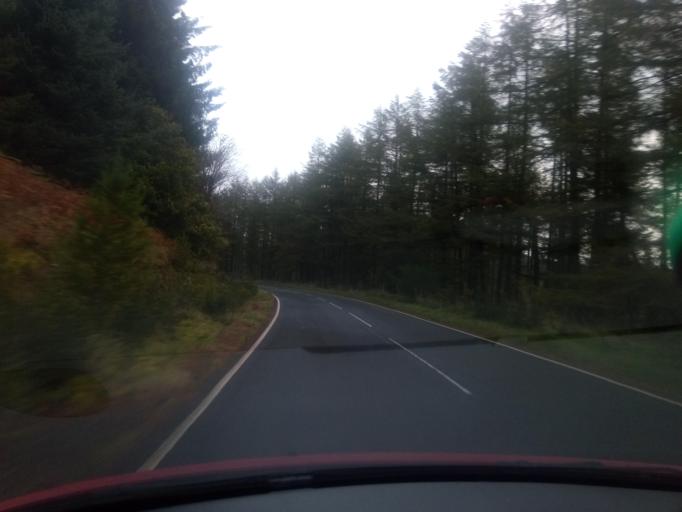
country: GB
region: Scotland
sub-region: The Scottish Borders
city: Hawick
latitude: 55.3330
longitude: -2.6487
